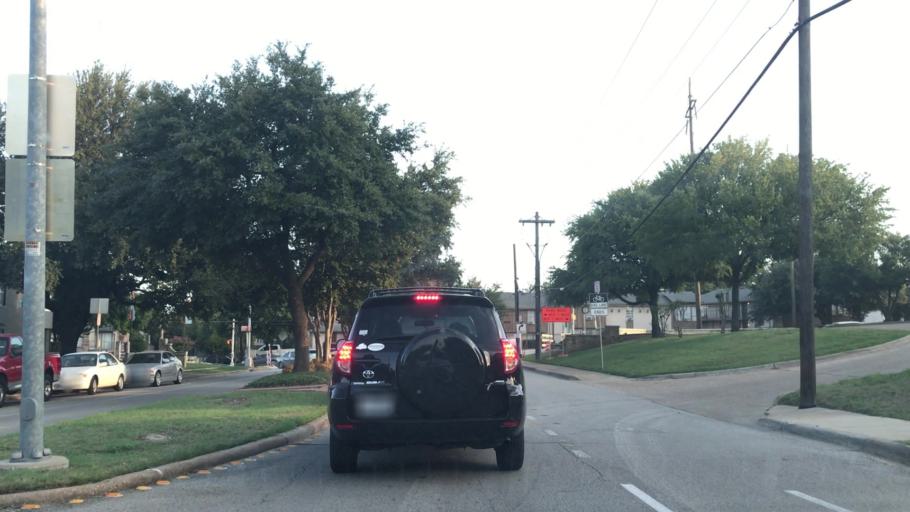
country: US
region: Texas
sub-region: Dallas County
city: Richardson
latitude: 32.9409
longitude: -96.7575
